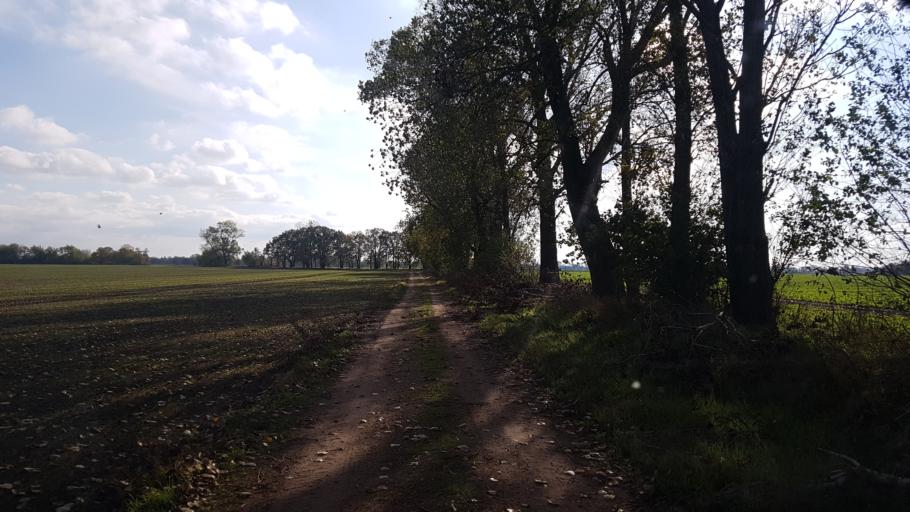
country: DE
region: Brandenburg
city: Schonewalde
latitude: 51.6881
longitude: 13.5767
